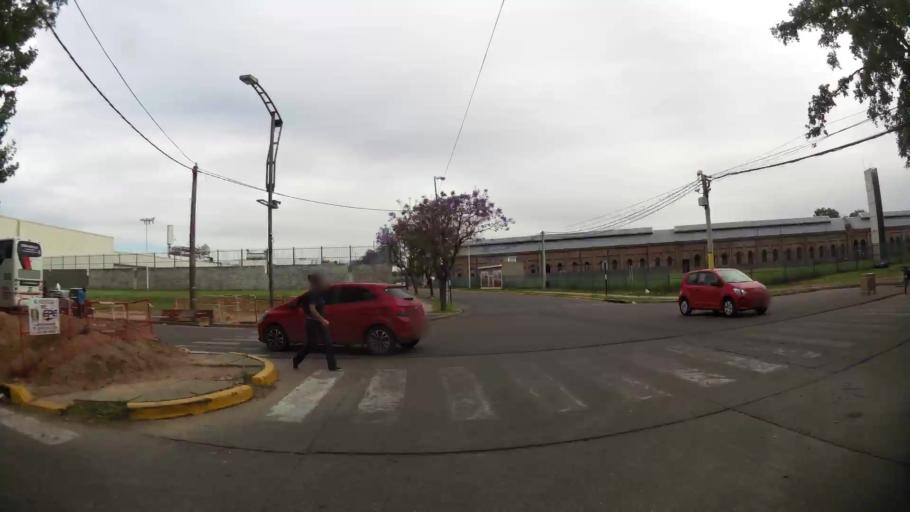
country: AR
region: Santa Fe
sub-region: Departamento de Rosario
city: Rosario
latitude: -32.9265
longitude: -60.6721
